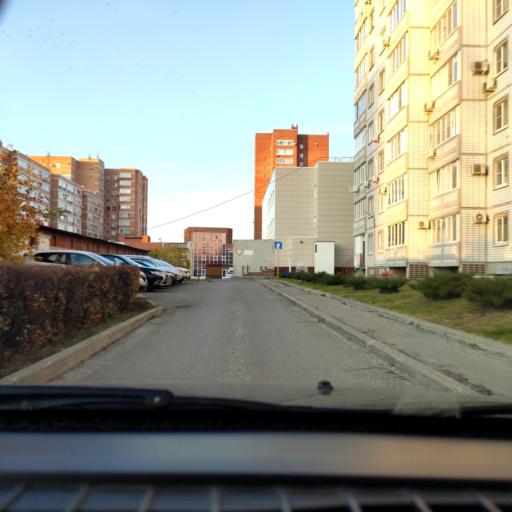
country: RU
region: Samara
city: Tol'yatti
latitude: 53.5151
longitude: 49.3034
